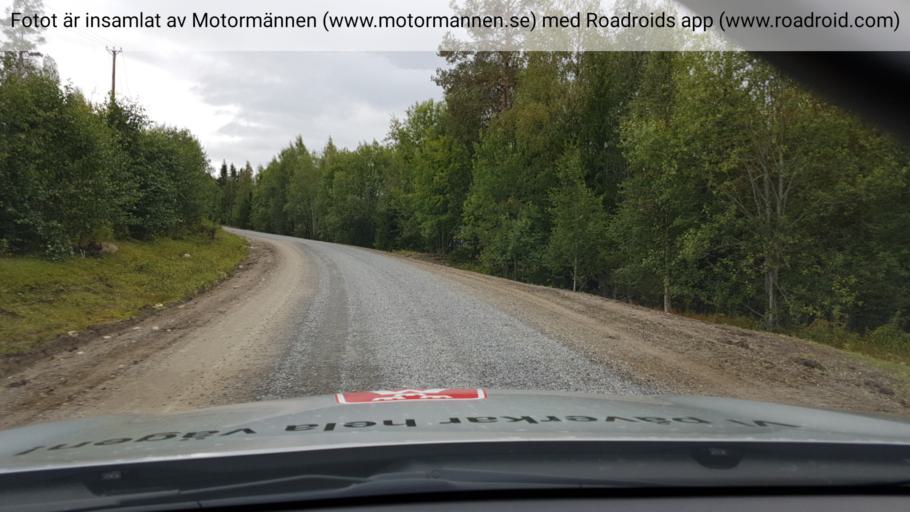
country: SE
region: Jaemtland
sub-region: Ragunda Kommun
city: Hammarstrand
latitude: 62.9081
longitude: 16.0933
